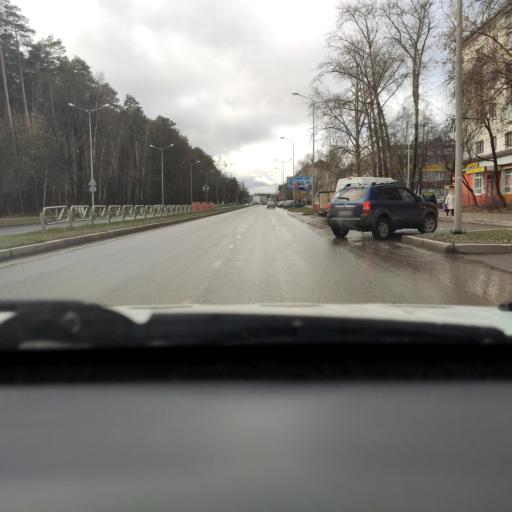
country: RU
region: Perm
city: Kultayevo
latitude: 58.0138
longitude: 55.9750
